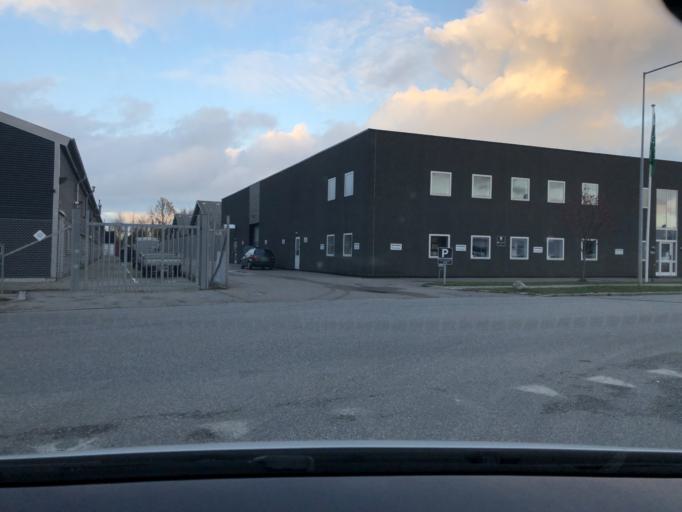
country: DK
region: Capital Region
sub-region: Tarnby Kommune
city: Tarnby
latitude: 55.6171
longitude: 12.6159
